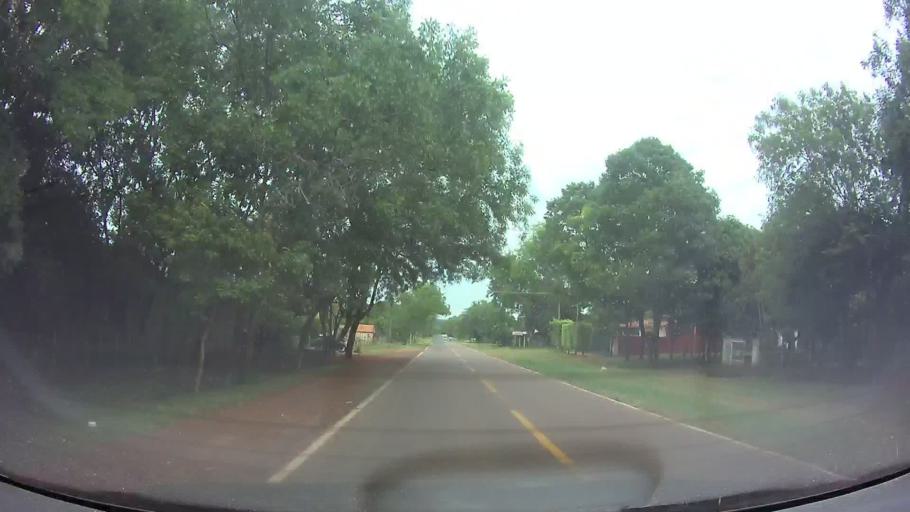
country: PY
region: Paraguari
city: Carapegua
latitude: -25.7938
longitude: -57.2058
